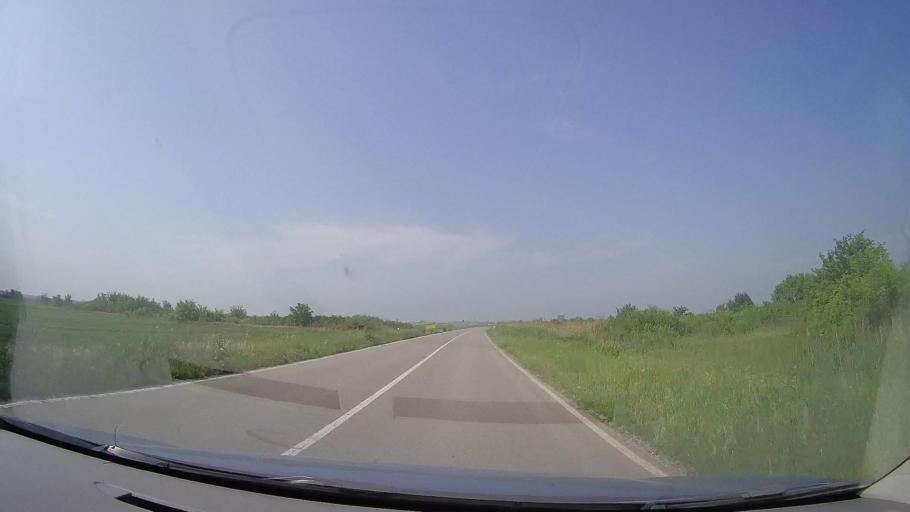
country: RS
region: Autonomna Pokrajina Vojvodina
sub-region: Srednjebanatski Okrug
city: Secanj
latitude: 45.3885
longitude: 20.8003
